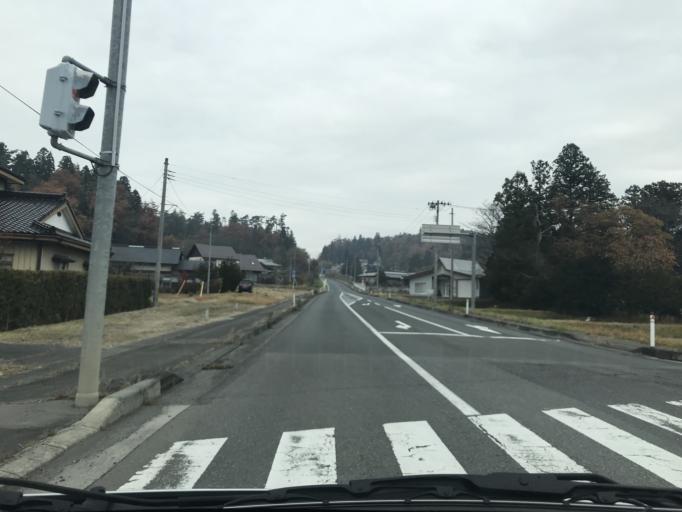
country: JP
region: Iwate
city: Mizusawa
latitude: 39.1608
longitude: 141.2010
